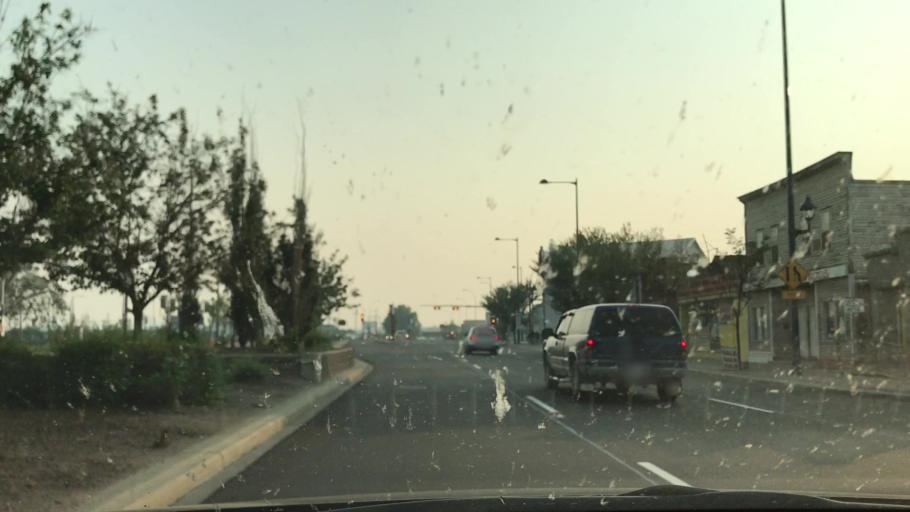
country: CA
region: Alberta
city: Edmonton
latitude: 53.5860
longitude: -113.4411
